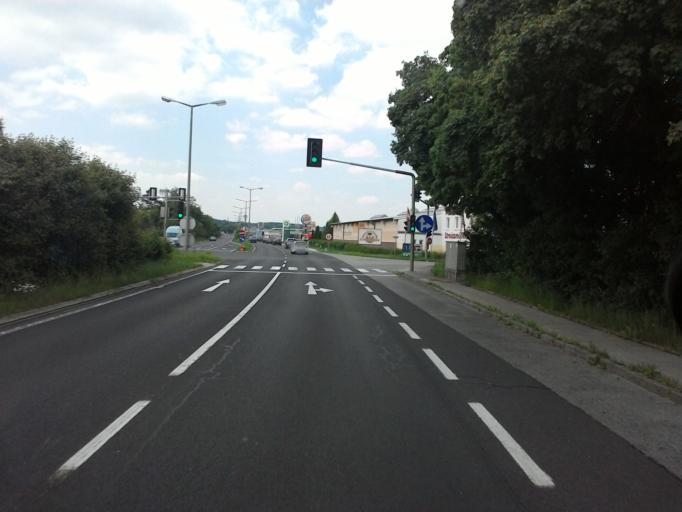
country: AT
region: Upper Austria
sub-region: Wels Stadt
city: Wels
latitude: 48.1791
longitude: 14.0276
